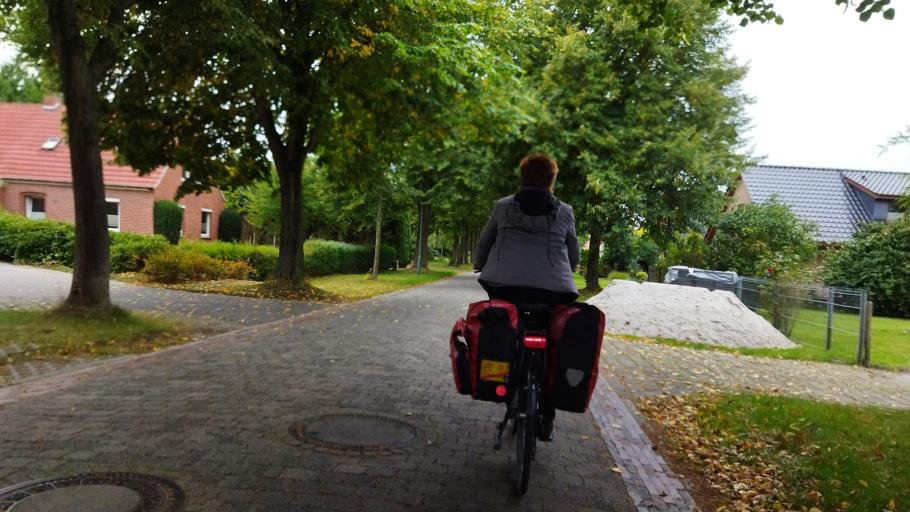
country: DE
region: Lower Saxony
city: Leer
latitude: 53.2624
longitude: 7.4343
